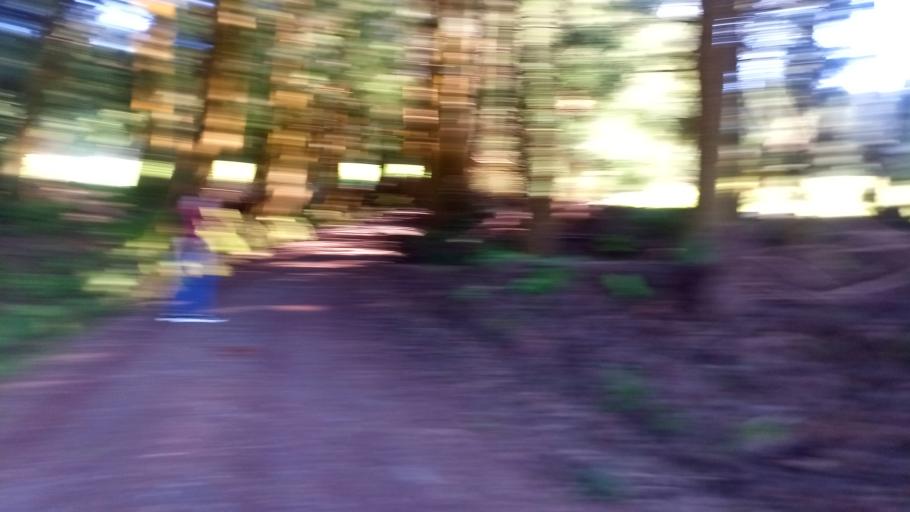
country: PT
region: Azores
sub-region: Praia da Vitoria
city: Biscoitos
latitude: 38.7164
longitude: -27.3416
